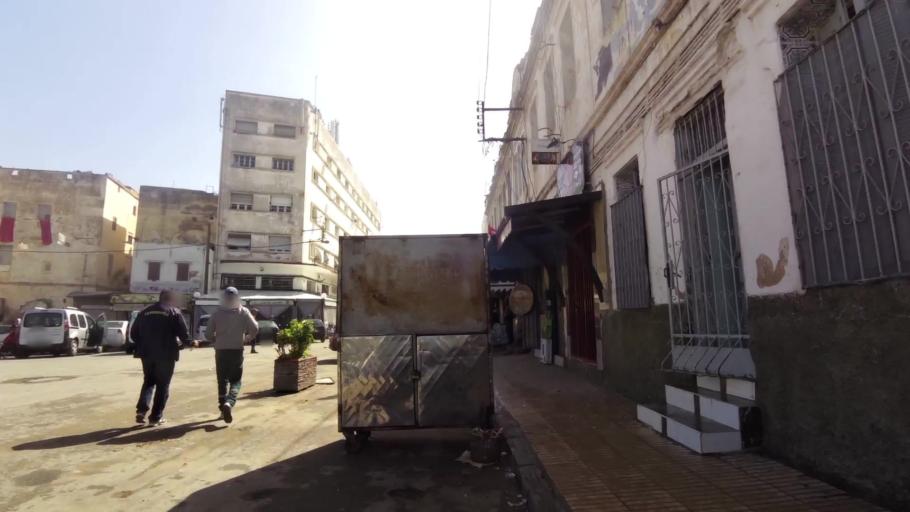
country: MA
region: Grand Casablanca
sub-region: Casablanca
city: Casablanca
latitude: 33.6034
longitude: -7.6280
